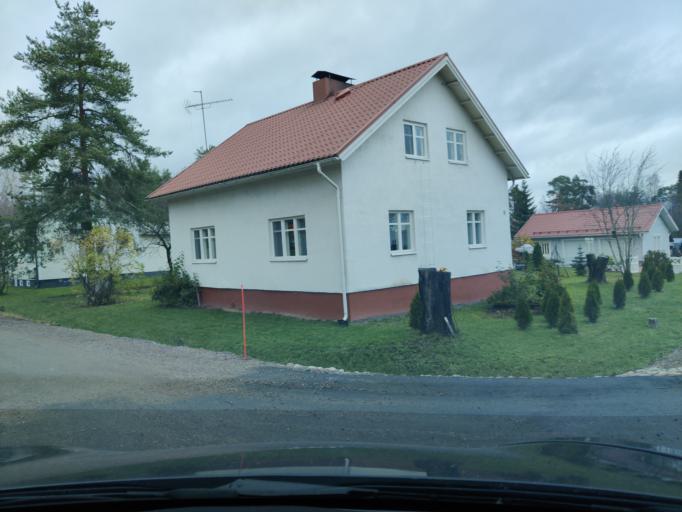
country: FI
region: Northern Savo
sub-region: Ylae-Savo
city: Kiuruvesi
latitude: 63.6484
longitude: 26.6334
